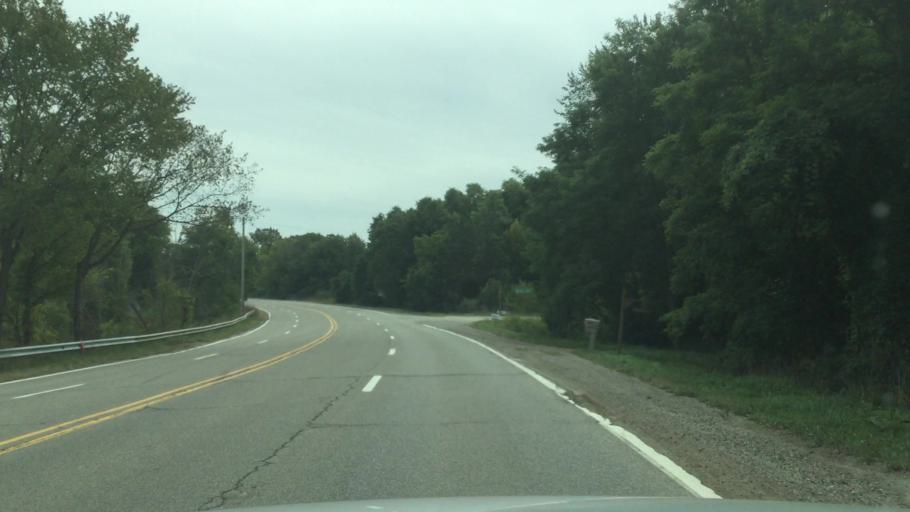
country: US
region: Michigan
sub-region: Oakland County
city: Holly
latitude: 42.8031
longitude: -83.5339
